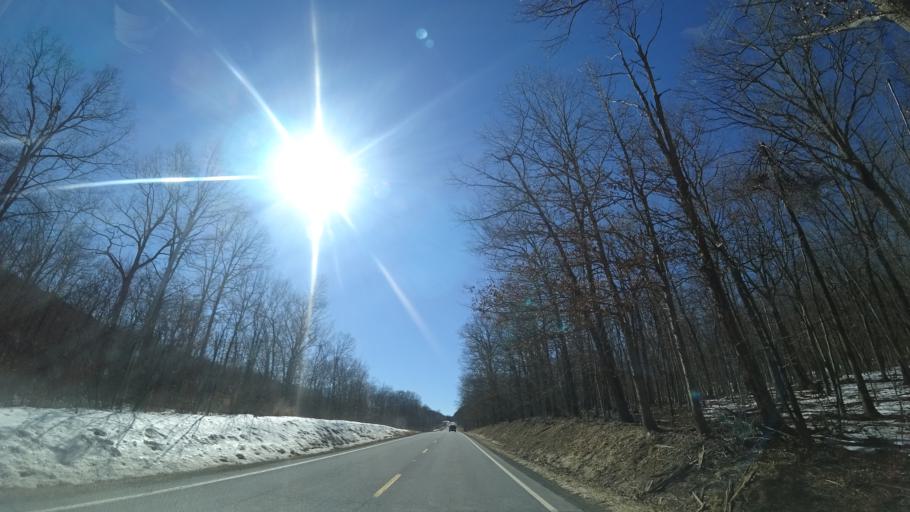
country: US
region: Virginia
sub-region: Shenandoah County
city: Strasburg
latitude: 39.0961
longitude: -78.4868
